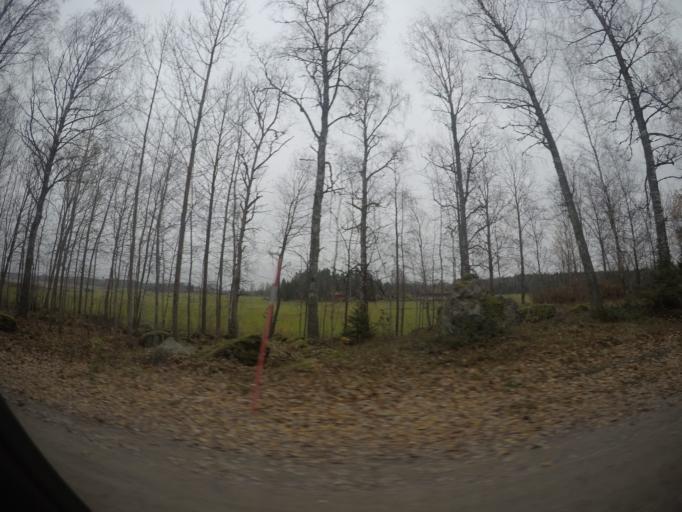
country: SE
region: Vaestmanland
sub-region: Kopings Kommun
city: Koping
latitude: 59.5929
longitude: 16.0849
